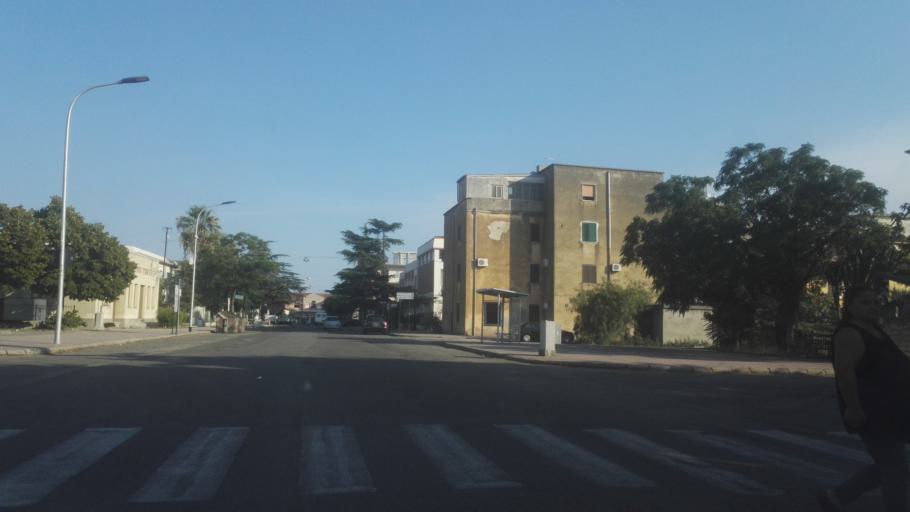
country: IT
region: Calabria
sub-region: Provincia di Reggio Calabria
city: Marina di Gioiosa Ionica
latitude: 38.3020
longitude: 16.3291
